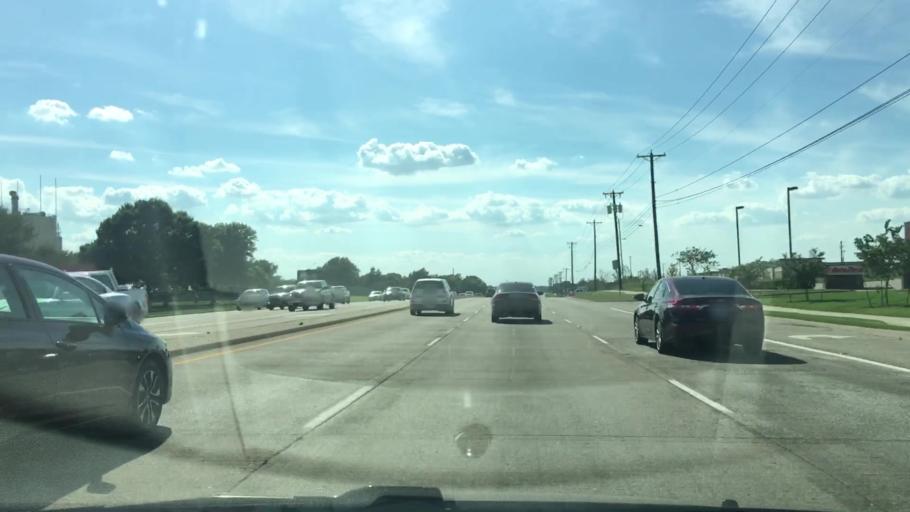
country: US
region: Texas
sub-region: Collin County
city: McKinney
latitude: 33.2171
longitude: -96.6537
